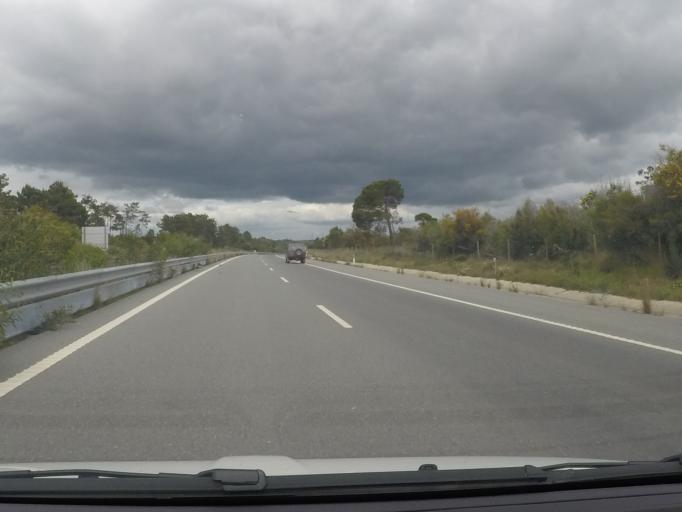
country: PT
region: Setubal
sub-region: Santiago do Cacem
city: Santo Andre
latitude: 37.9850
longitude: -8.7828
